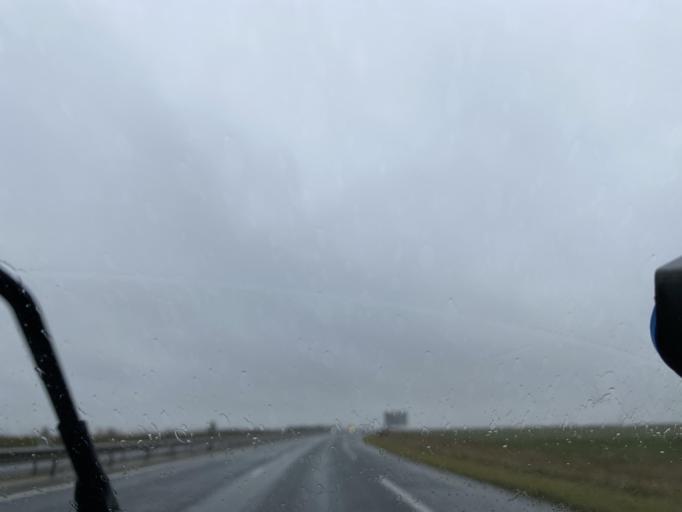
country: FR
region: Centre
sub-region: Departement d'Eure-et-Loir
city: Bailleau-l'Eveque
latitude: 48.5509
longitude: 1.4475
